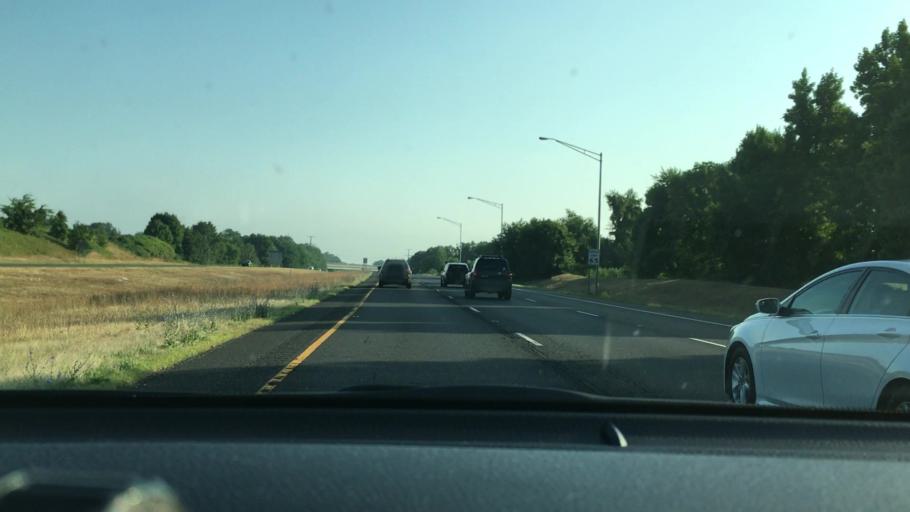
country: US
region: New Jersey
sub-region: Gloucester County
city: Richwood
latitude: 39.7235
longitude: -75.1527
